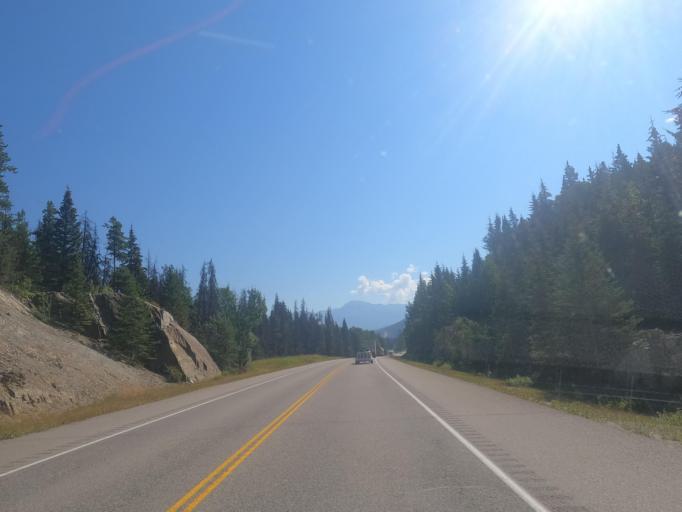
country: CA
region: Alberta
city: Jasper Park Lodge
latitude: 52.8604
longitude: -118.1794
